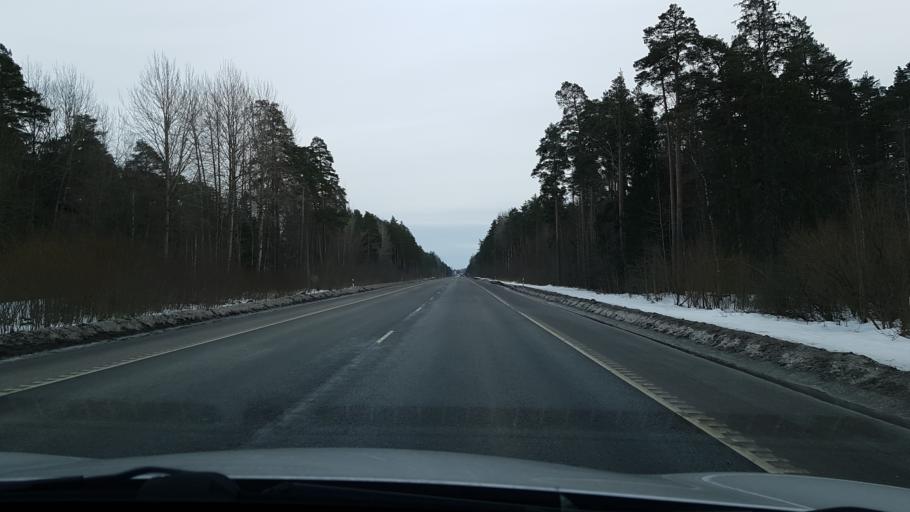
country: EE
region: Tartu
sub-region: Tartu linn
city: Tartu
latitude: 58.3992
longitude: 26.6588
